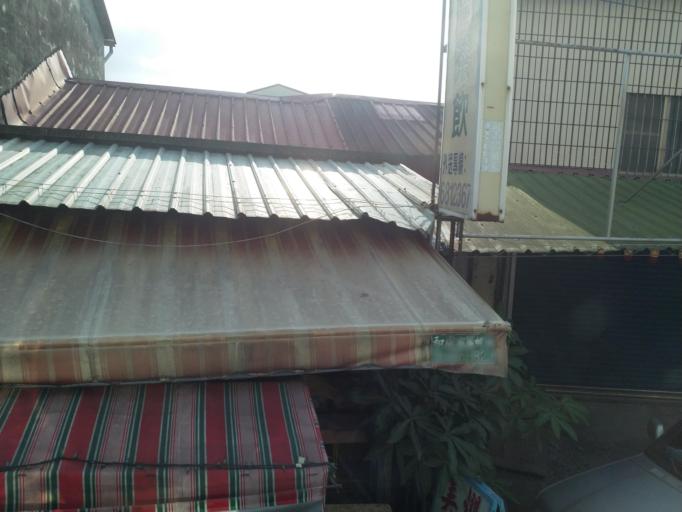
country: TW
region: Taiwan
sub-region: Pingtung
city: Pingtung
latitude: 22.8975
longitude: 120.5430
